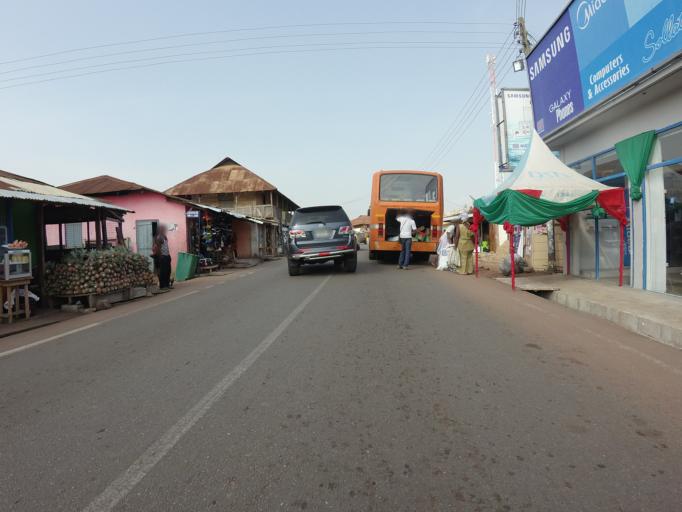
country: GH
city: Akropong
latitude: 6.1036
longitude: -0.0153
